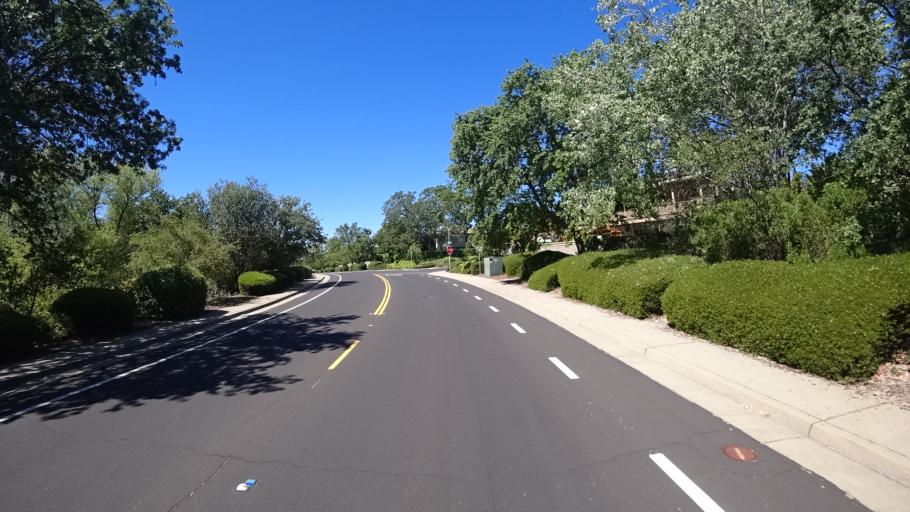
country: US
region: California
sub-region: Placer County
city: Rocklin
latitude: 38.7723
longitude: -121.2240
